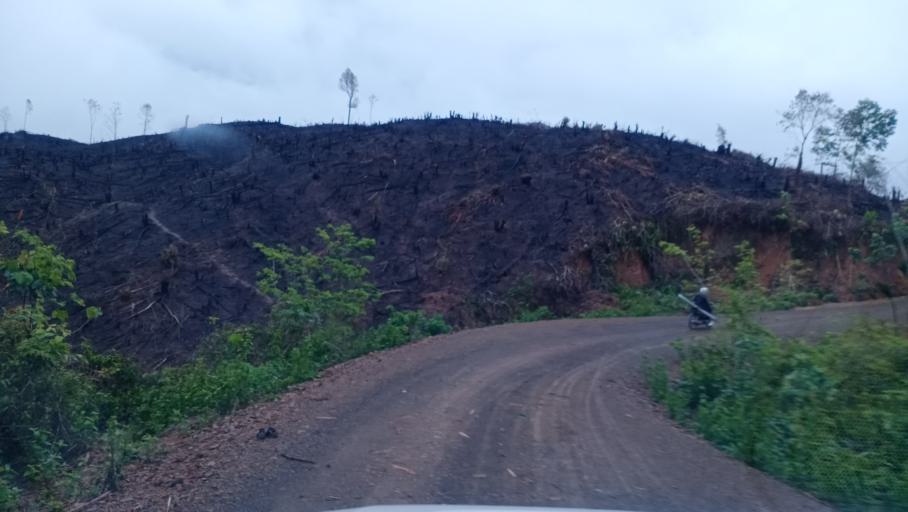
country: LA
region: Phongsali
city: Khoa
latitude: 21.3030
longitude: 102.7054
